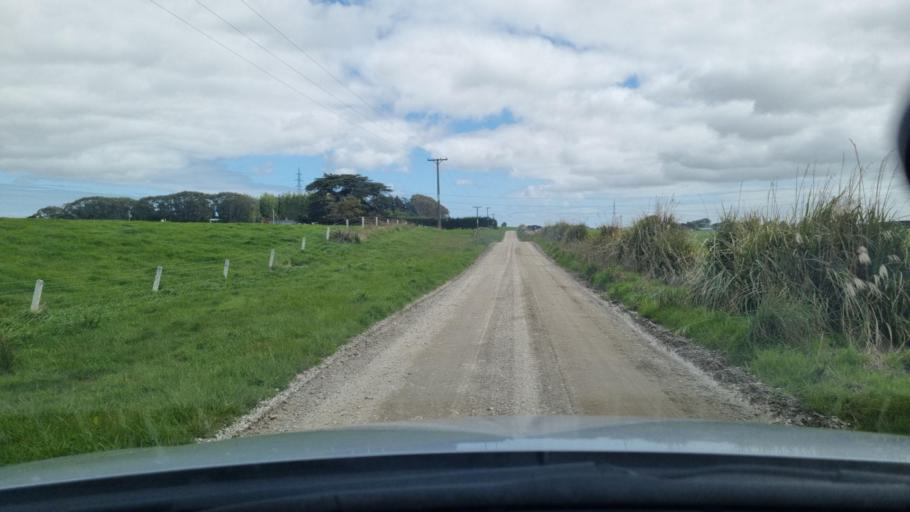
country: NZ
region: Southland
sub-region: Invercargill City
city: Invercargill
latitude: -46.4557
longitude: 168.4539
